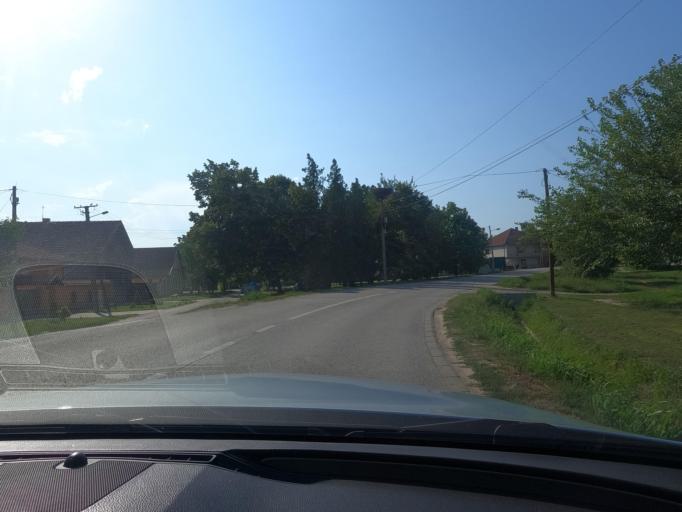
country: RS
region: Autonomna Pokrajina Vojvodina
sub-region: Juznobacki Okrug
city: Kovilj
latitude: 45.2194
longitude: 20.0205
